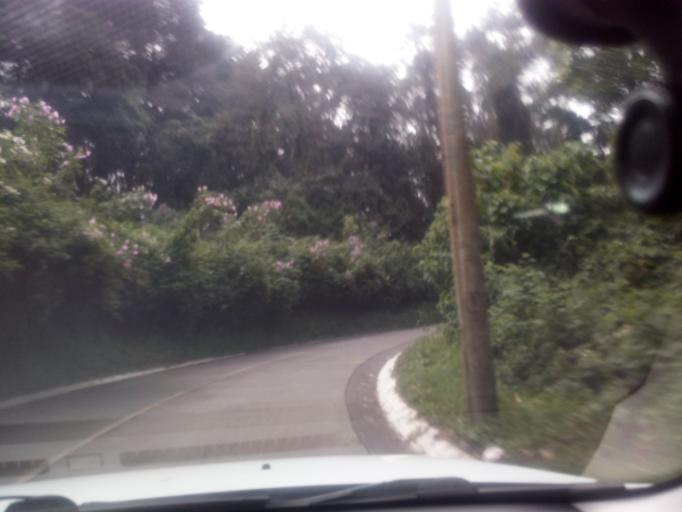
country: GT
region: Sacatepequez
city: San Bartolome Milpas Altas
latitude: 14.5972
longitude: -90.6836
